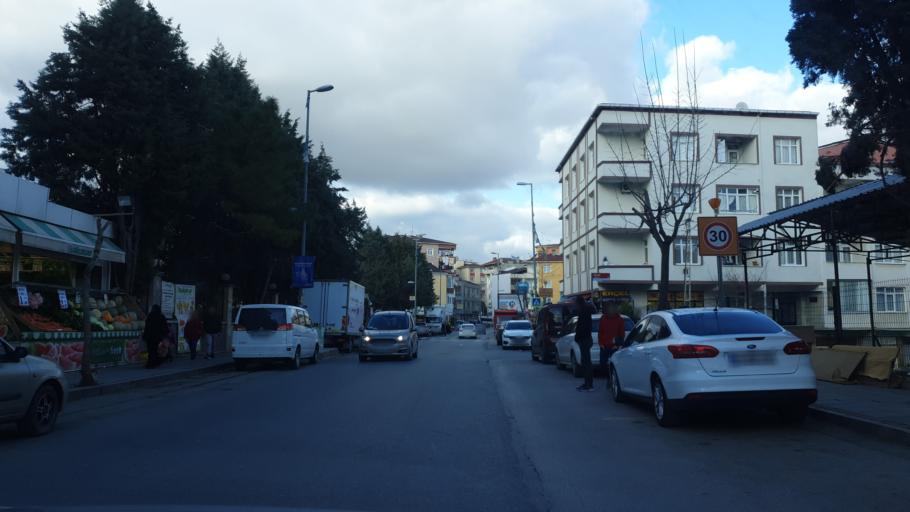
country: TR
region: Istanbul
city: Pendik
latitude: 40.8776
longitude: 29.2737
